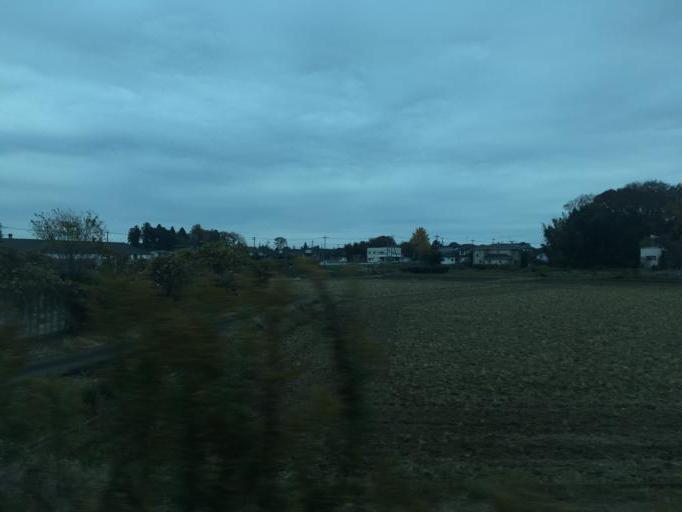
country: JP
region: Ibaraki
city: Shimodate
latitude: 36.3003
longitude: 139.9509
